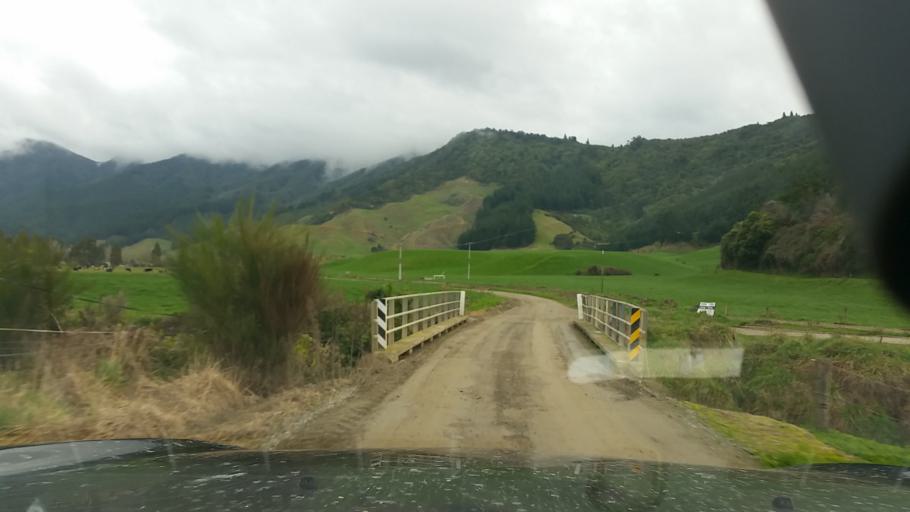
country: NZ
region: Marlborough
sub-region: Marlborough District
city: Picton
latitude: -41.2933
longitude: 173.8574
